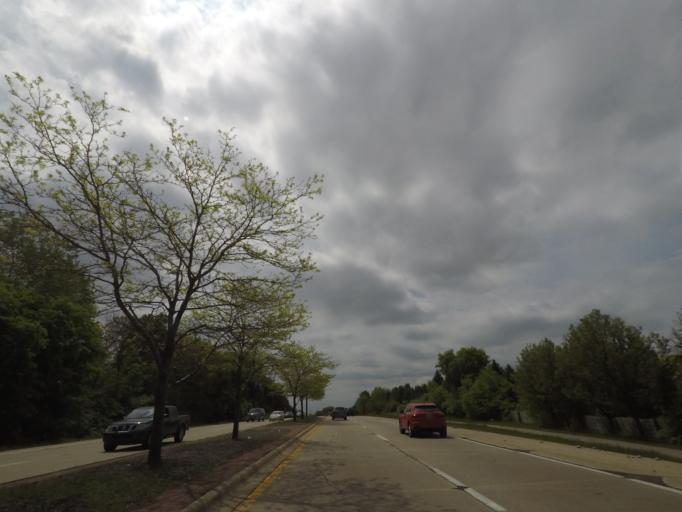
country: US
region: Illinois
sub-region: Winnebago County
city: Cherry Valley
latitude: 42.2883
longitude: -88.9805
